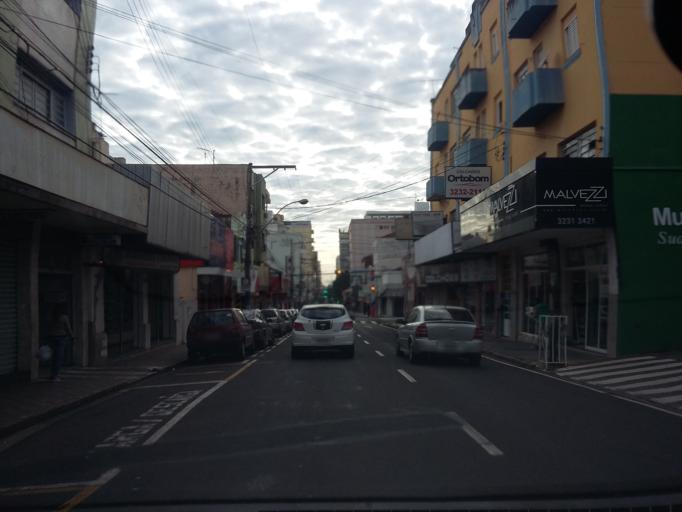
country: BR
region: Sao Paulo
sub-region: Sao Jose Do Rio Preto
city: Sao Jose do Rio Preto
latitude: -20.8151
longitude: -49.3846
